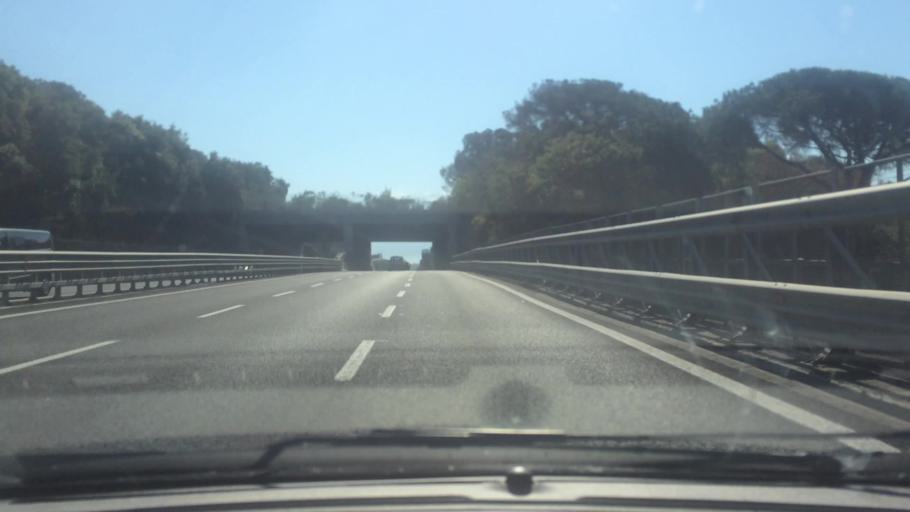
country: IT
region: Campania
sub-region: Provincia di Napoli
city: Ercolano
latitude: 40.7980
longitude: 14.3720
